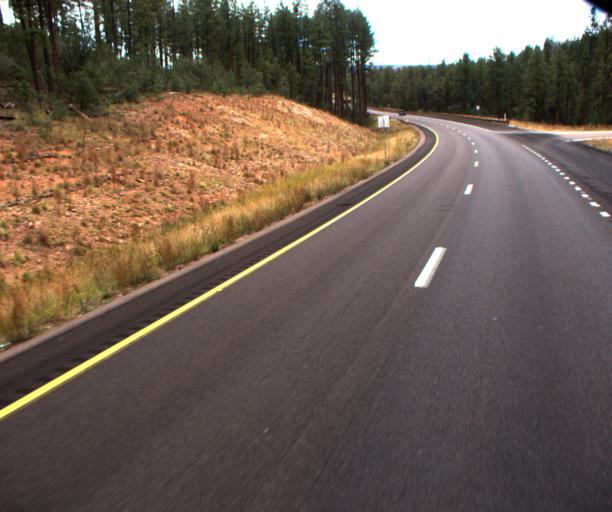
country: US
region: Arizona
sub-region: Gila County
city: Star Valley
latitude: 34.3072
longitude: -111.1085
